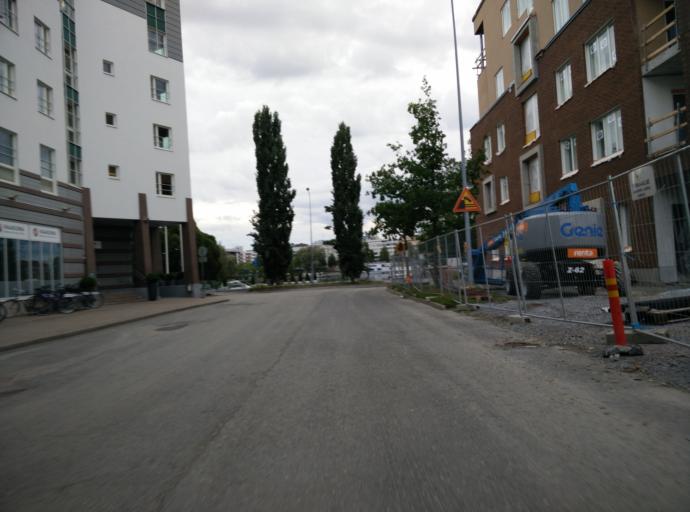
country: FI
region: Haeme
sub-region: Haemeenlinna
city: Haemeenlinna
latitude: 61.0010
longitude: 24.4756
